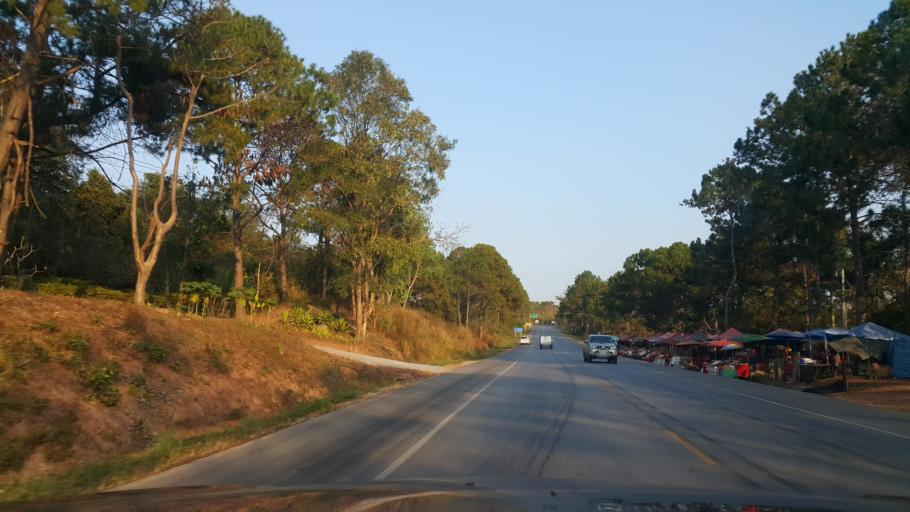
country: TH
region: Loei
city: Phu Ruea
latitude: 17.4477
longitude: 101.4885
